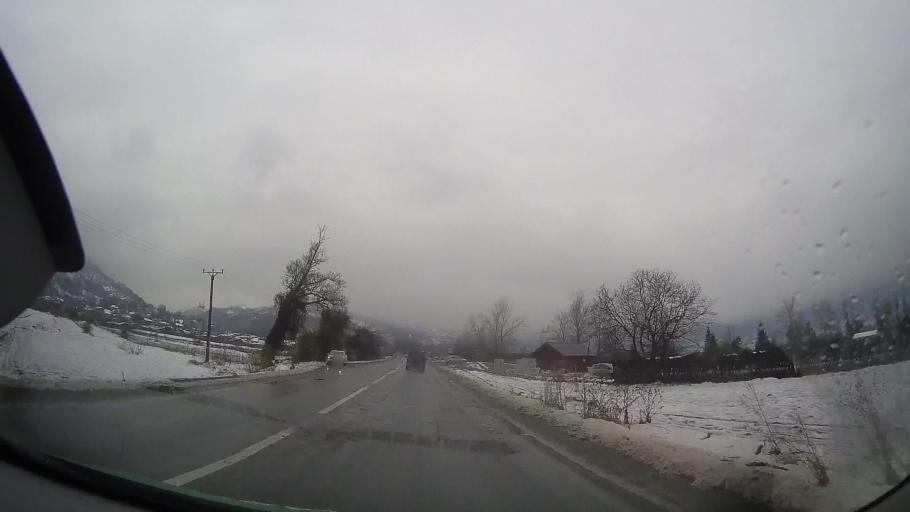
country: RO
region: Neamt
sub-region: Comuna Pangarati
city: Stejaru
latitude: 46.9217
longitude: 26.1894
